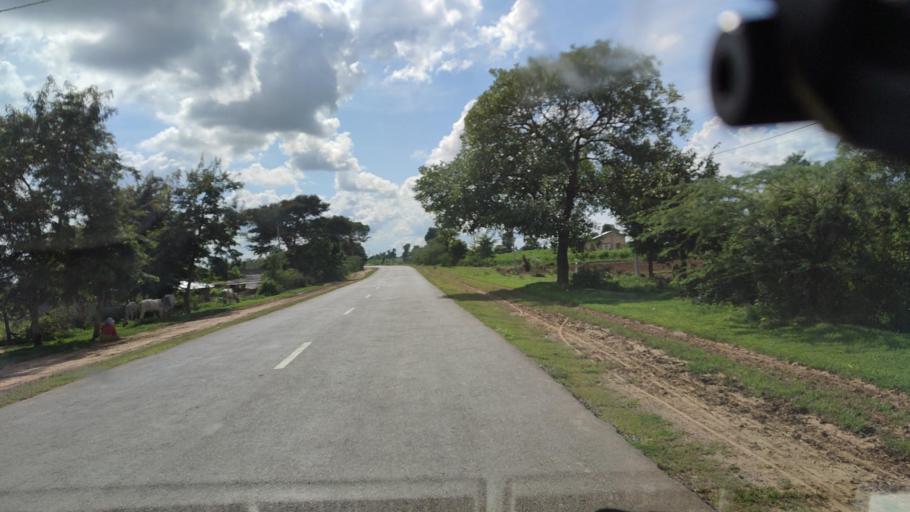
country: MM
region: Mandalay
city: Meiktila
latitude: 20.7949
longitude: 95.5533
